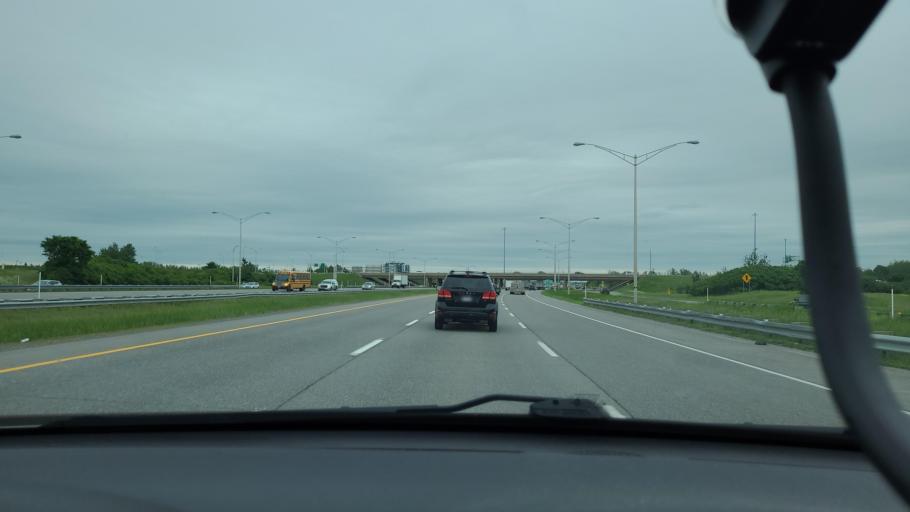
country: CA
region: Quebec
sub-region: Laval
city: Laval
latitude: 45.6031
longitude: -73.7015
